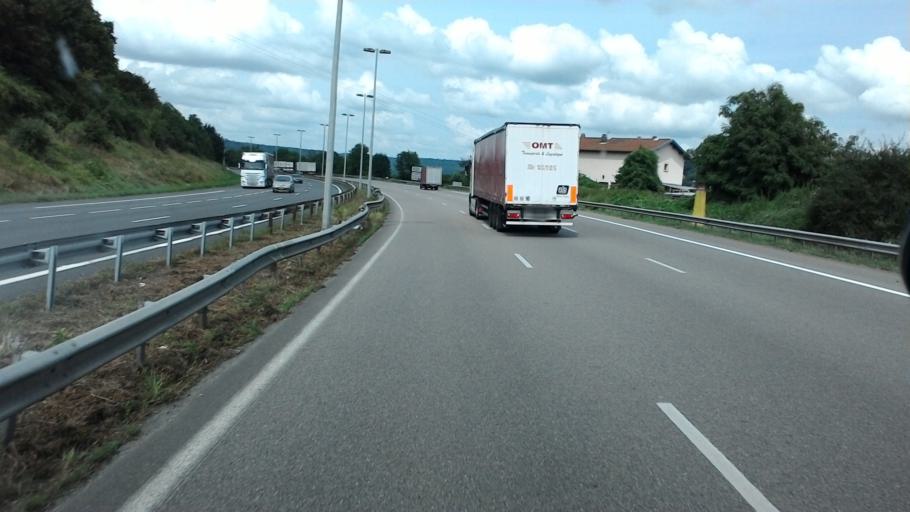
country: FR
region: Lorraine
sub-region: Departement de Meurthe-et-Moselle
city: Maxeville
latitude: 48.7209
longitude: 6.1682
